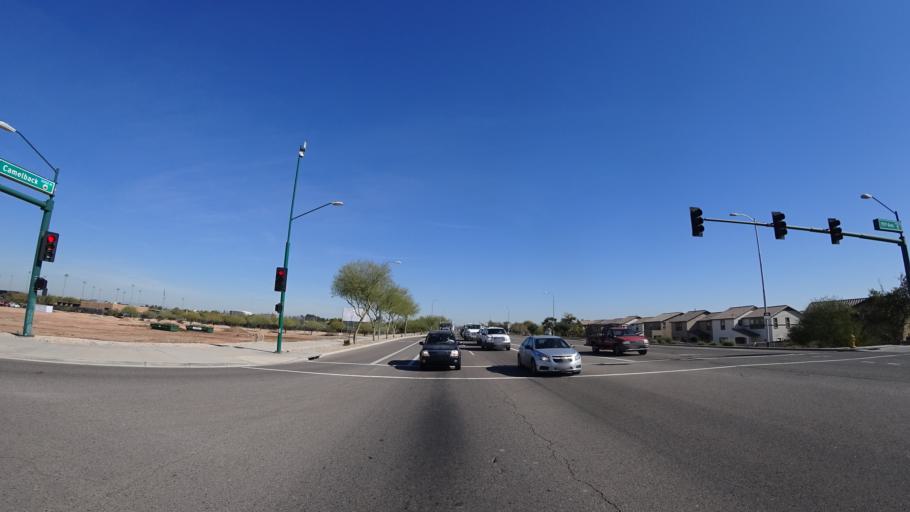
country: US
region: Arizona
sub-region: Maricopa County
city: Litchfield Park
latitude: 33.5079
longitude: -112.2985
